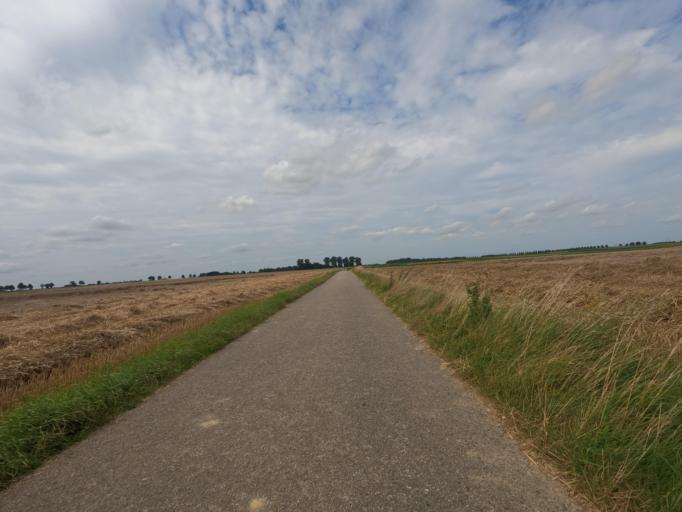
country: DE
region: North Rhine-Westphalia
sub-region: Regierungsbezirk Koln
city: Ubach-Palenberg
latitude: 50.9356
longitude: 6.1472
